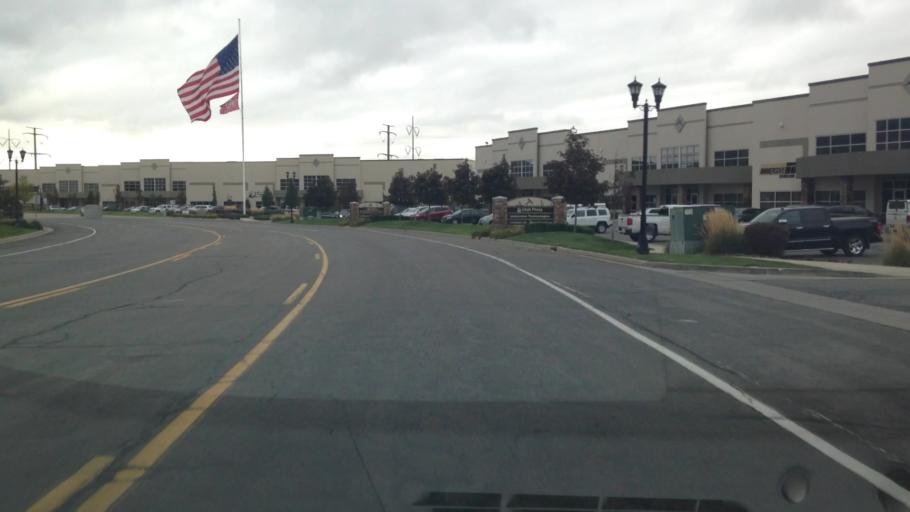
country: US
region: Utah
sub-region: Salt Lake County
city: South Jordan
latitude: 40.5746
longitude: -111.9063
